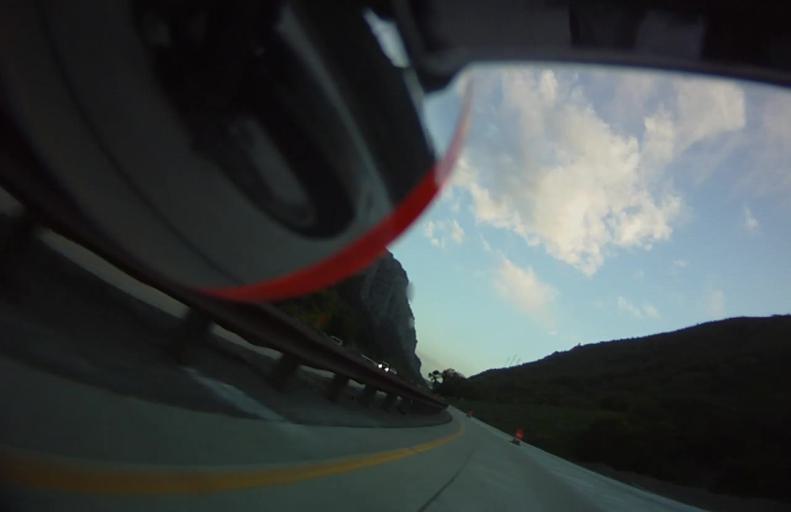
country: US
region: Utah
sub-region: Utah County
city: Orem
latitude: 40.3563
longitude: -111.5776
